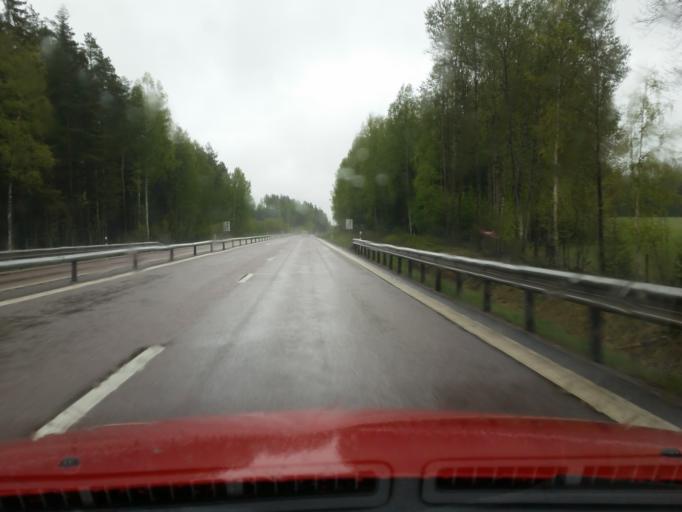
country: SE
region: Dalarna
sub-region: Hedemora Kommun
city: Hedemora
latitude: 60.3206
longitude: 15.9020
